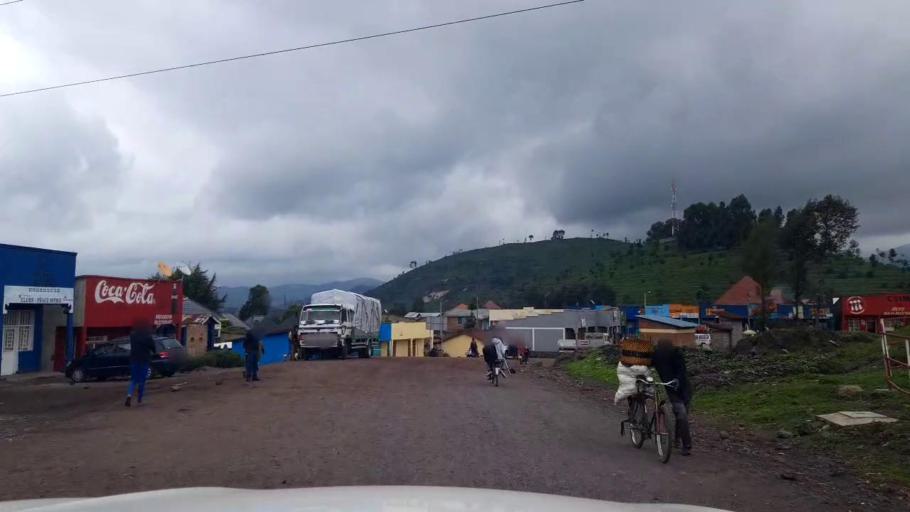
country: RW
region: Northern Province
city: Musanze
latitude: -1.6104
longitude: 29.4521
